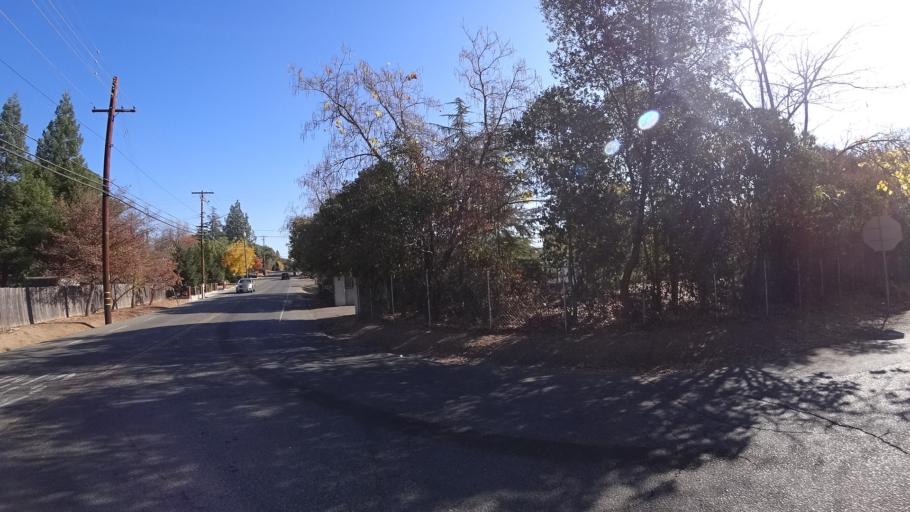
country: US
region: California
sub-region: Sacramento County
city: Citrus Heights
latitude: 38.6928
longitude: -121.2833
